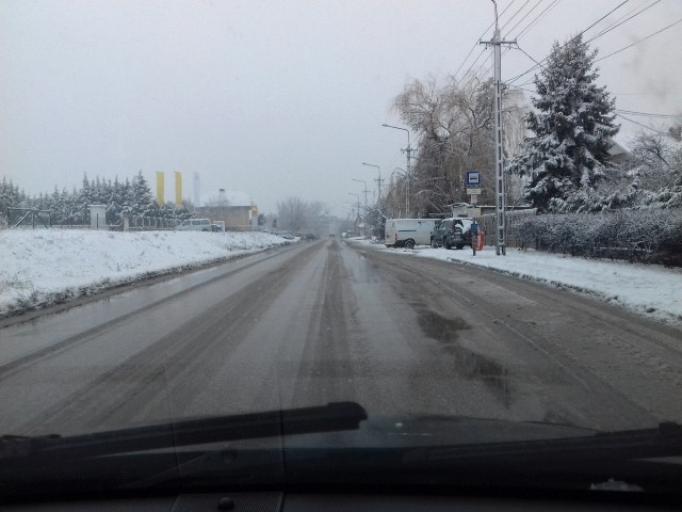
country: HU
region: Pest
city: Fot
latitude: 47.6216
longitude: 19.1886
